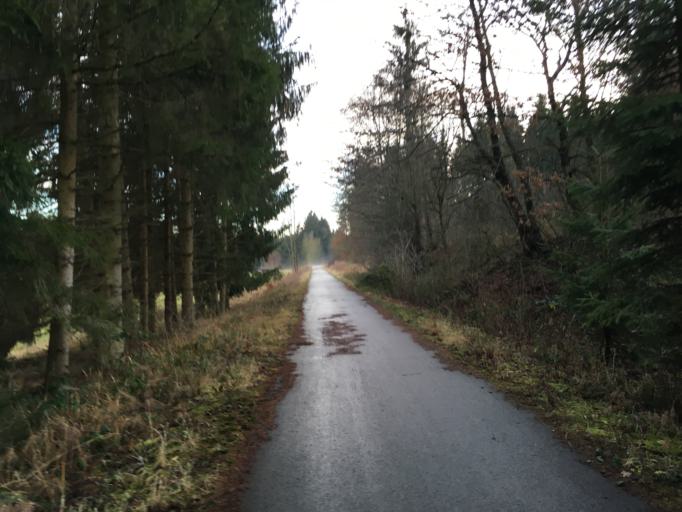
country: DE
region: Bavaria
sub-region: Swabia
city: Wald
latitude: 47.9860
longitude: 10.2857
